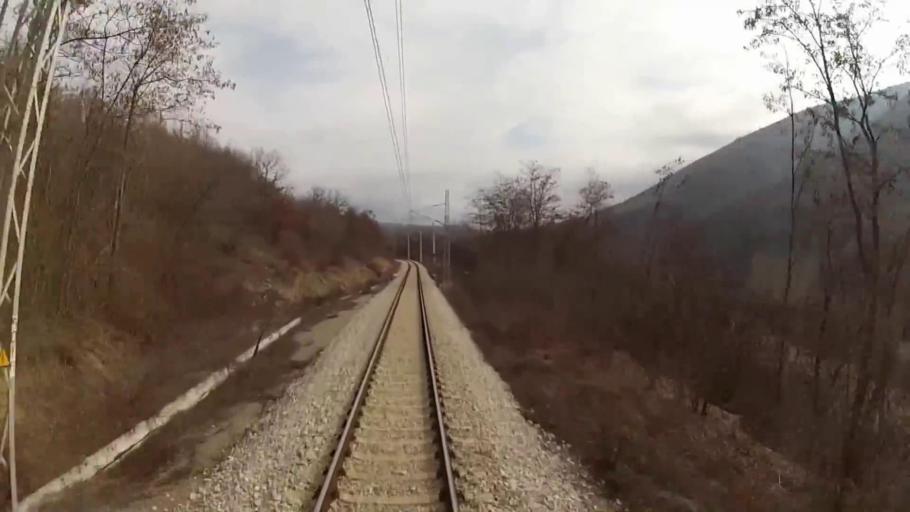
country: BG
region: Sofiya
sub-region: Obshtina Mirkovo
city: Mirkovo
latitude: 42.6898
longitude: 23.8501
